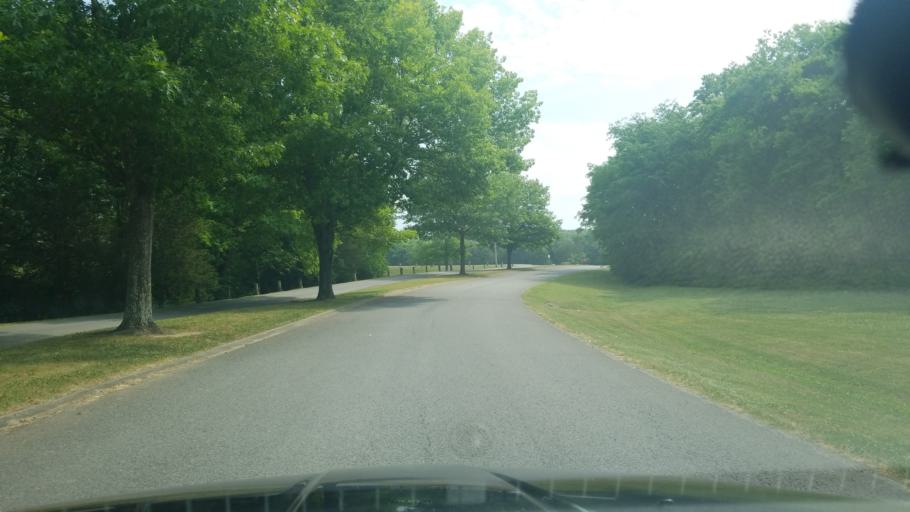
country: US
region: Tennessee
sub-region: Davidson County
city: Goodlettsville
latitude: 36.2695
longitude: -86.7461
